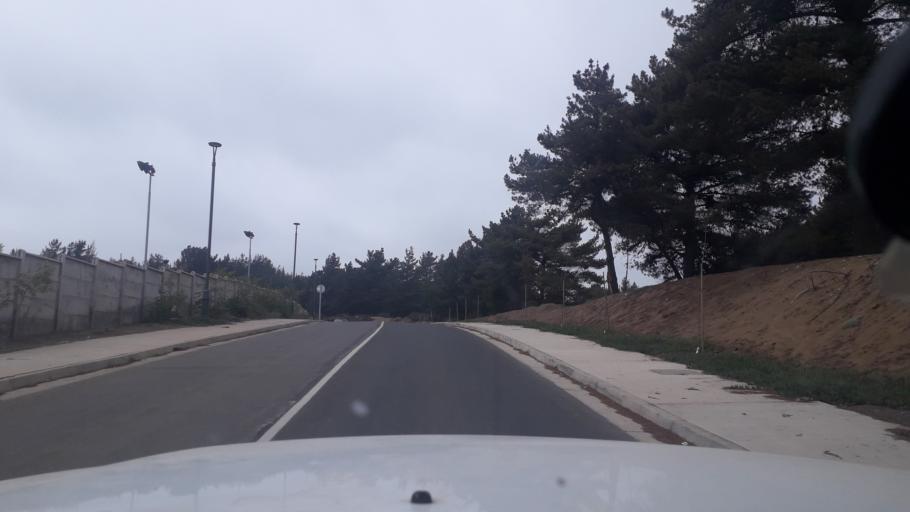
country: CL
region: Valparaiso
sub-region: Provincia de Valparaiso
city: Vina del Mar
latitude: -32.9475
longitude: -71.5337
